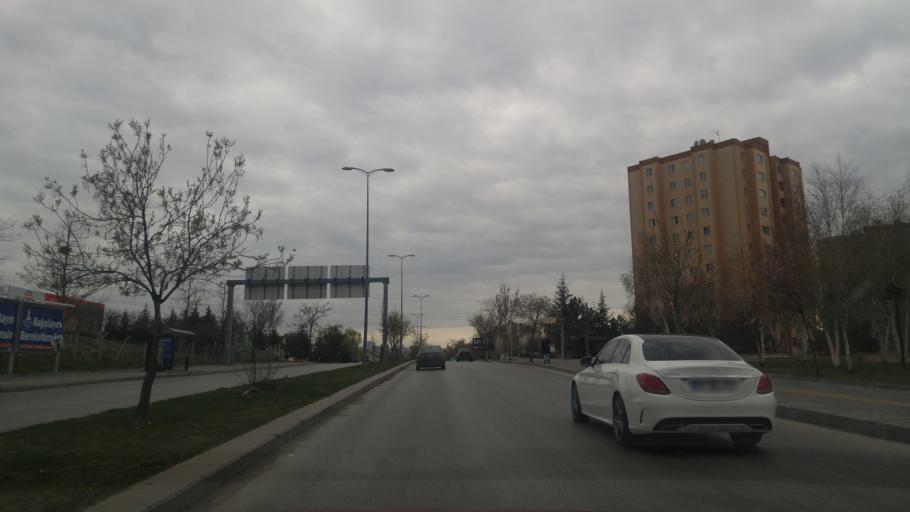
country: TR
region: Ankara
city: Etimesgut
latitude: 39.8833
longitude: 32.6901
